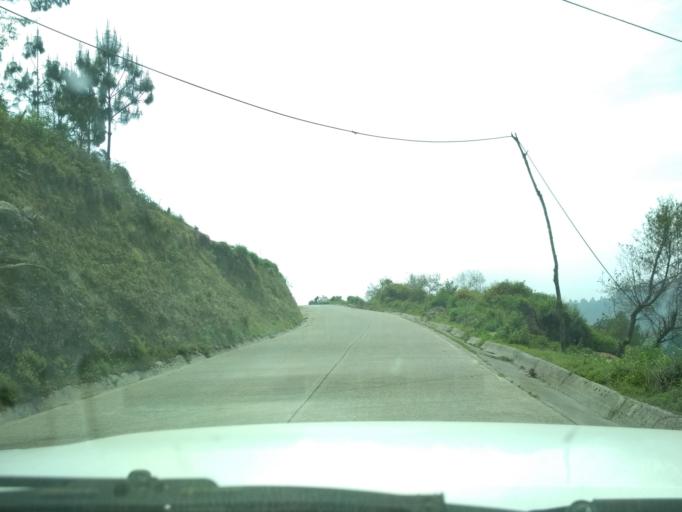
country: MX
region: Veracruz
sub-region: Mariano Escobedo
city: San Isidro el Berro
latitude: 18.9756
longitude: -97.2102
